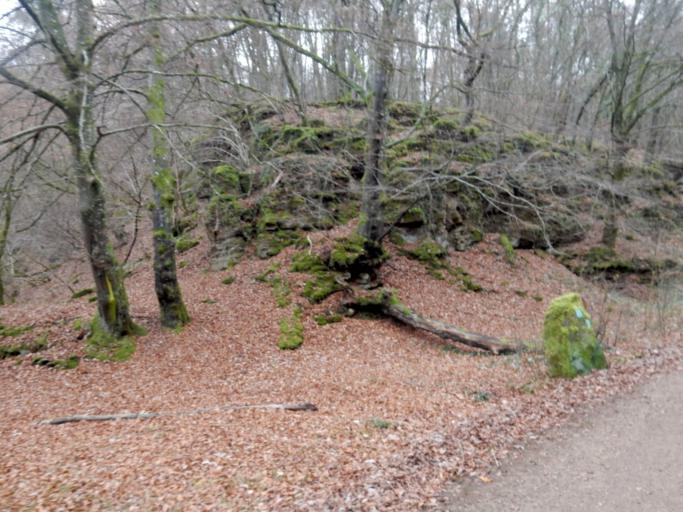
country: LU
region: Luxembourg
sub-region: Canton d'Esch-sur-Alzette
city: Dudelange
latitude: 49.4686
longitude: 6.0662
